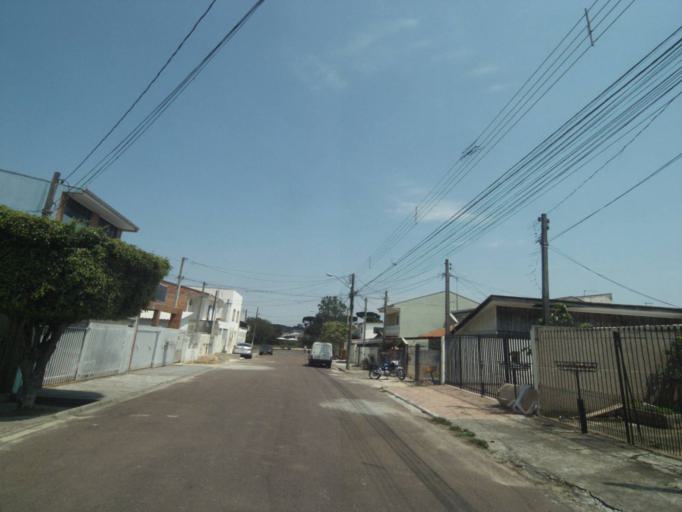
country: BR
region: Parana
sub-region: Sao Jose Dos Pinhais
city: Sao Jose dos Pinhais
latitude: -25.5215
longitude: -49.2671
